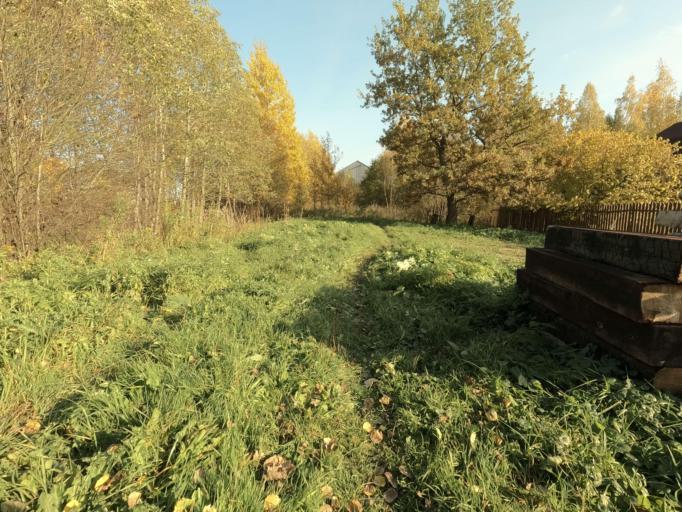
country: RU
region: Leningrad
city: Mga
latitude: 59.7473
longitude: 31.0738
